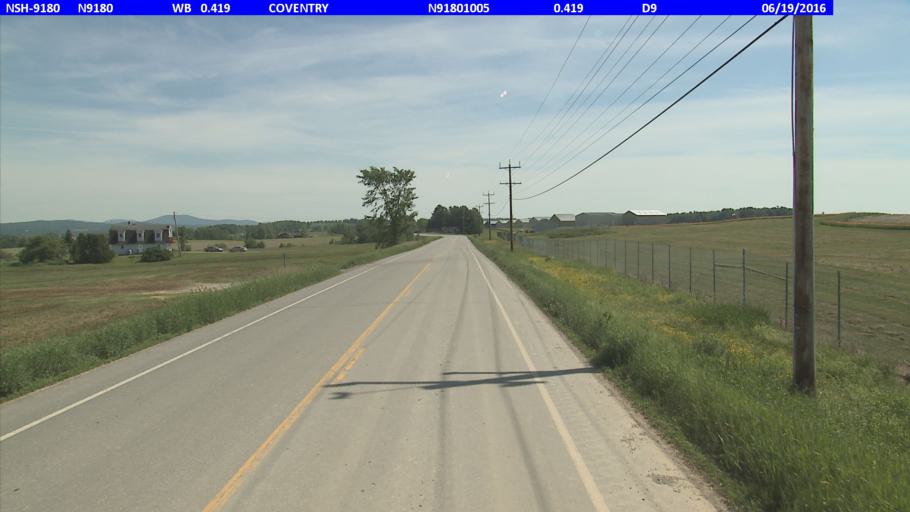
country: US
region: Vermont
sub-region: Orleans County
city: Newport
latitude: 44.8949
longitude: -72.2252
